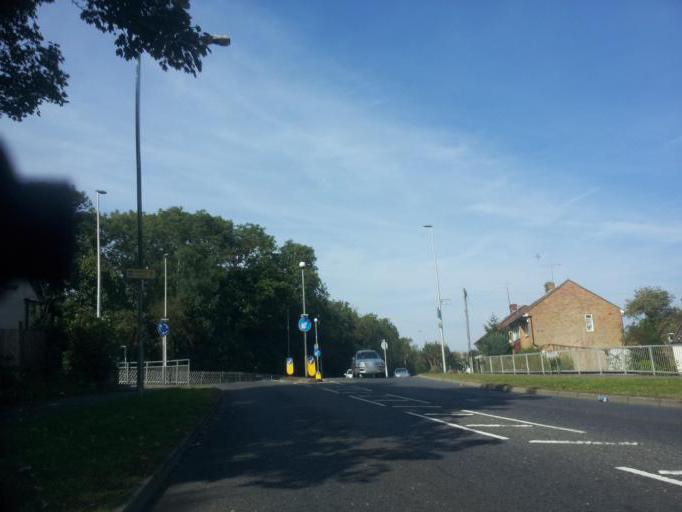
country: GB
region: England
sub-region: Kent
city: Rainham
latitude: 51.3533
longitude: 0.5734
